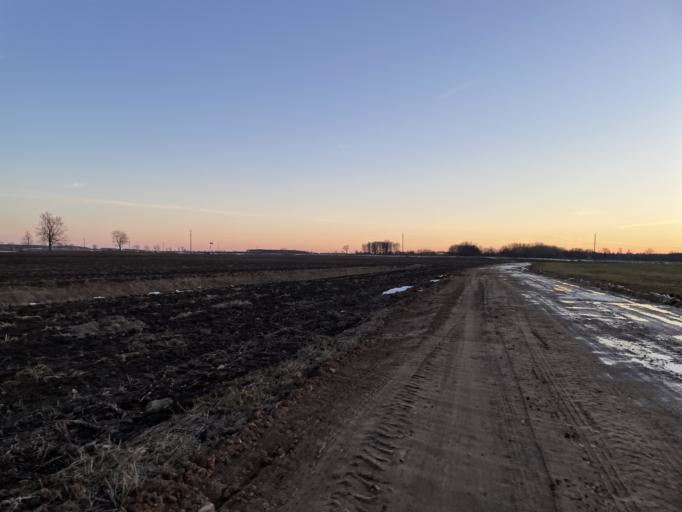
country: BY
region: Minsk
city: Nyasvizh
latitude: 53.2070
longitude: 26.6786
